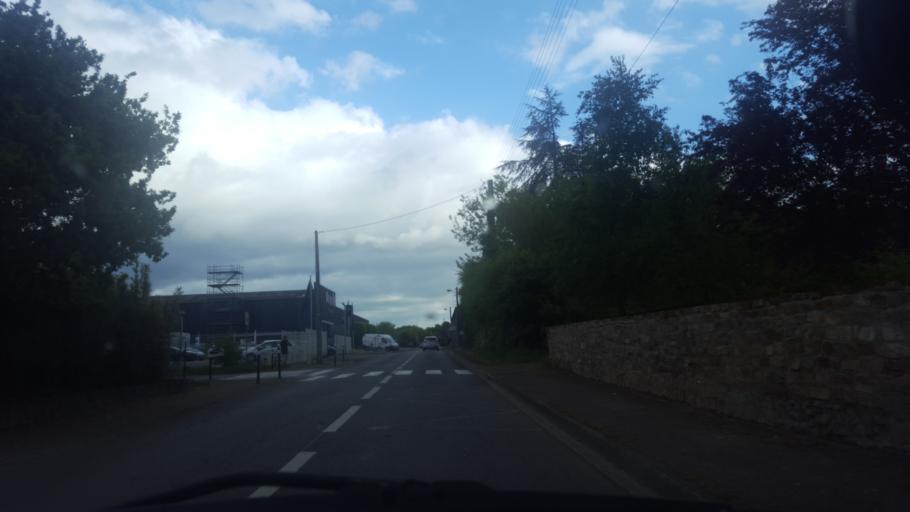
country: FR
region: Pays de la Loire
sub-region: Departement de la Loire-Atlantique
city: Saint-Philbert-de-Grand-Lieu
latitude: 47.0302
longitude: -1.6352
